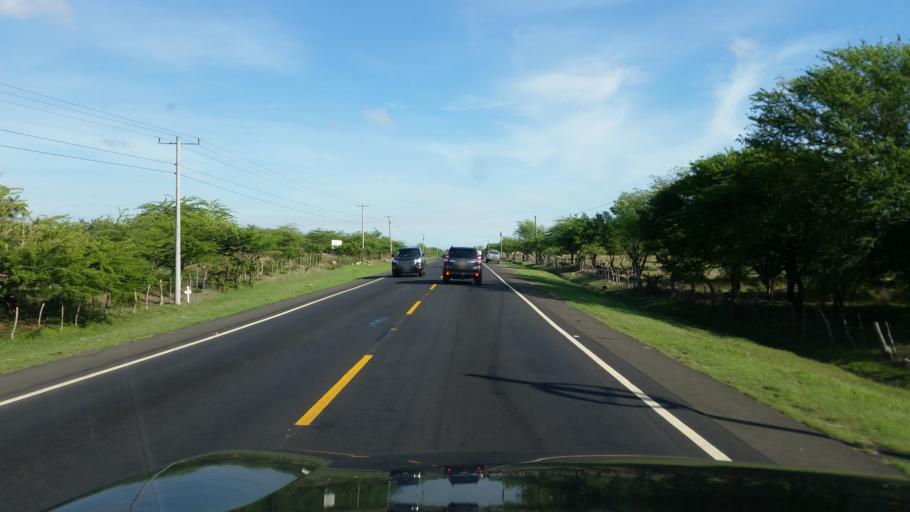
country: NI
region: Leon
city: La Paz Centro
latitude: 12.2729
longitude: -86.7420
